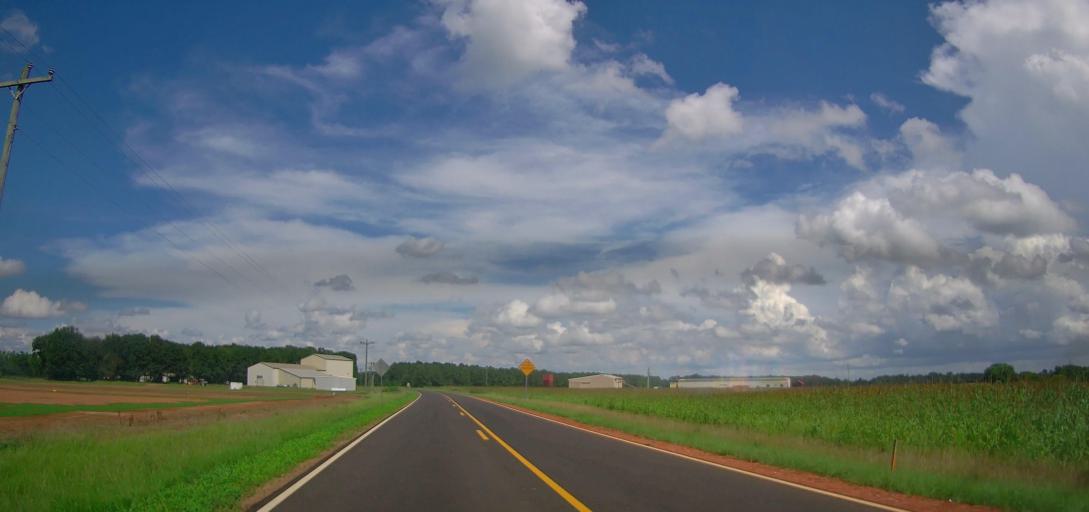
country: US
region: Georgia
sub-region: Macon County
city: Marshallville
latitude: 32.4628
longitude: -83.9072
